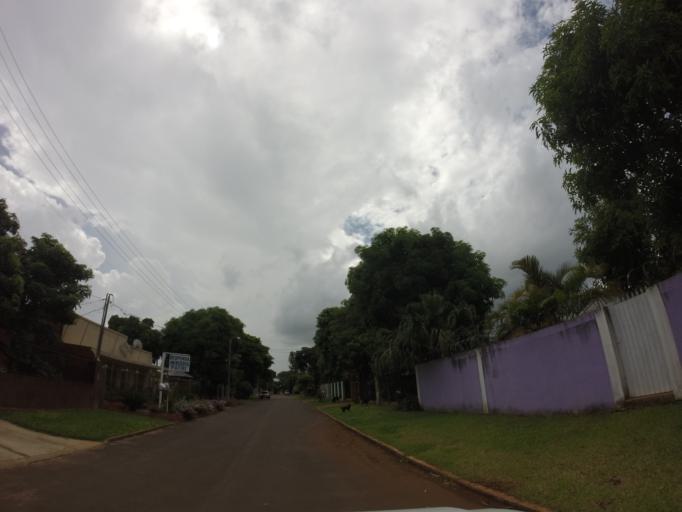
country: PY
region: Alto Parana
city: Ciudad del Este
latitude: -25.4168
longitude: -54.6261
